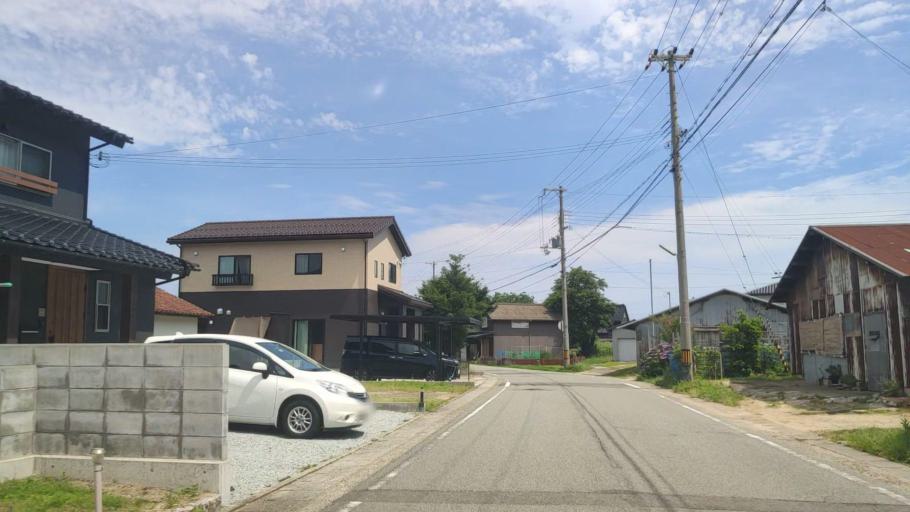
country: JP
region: Hyogo
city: Toyooka
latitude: 35.6544
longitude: 134.7629
